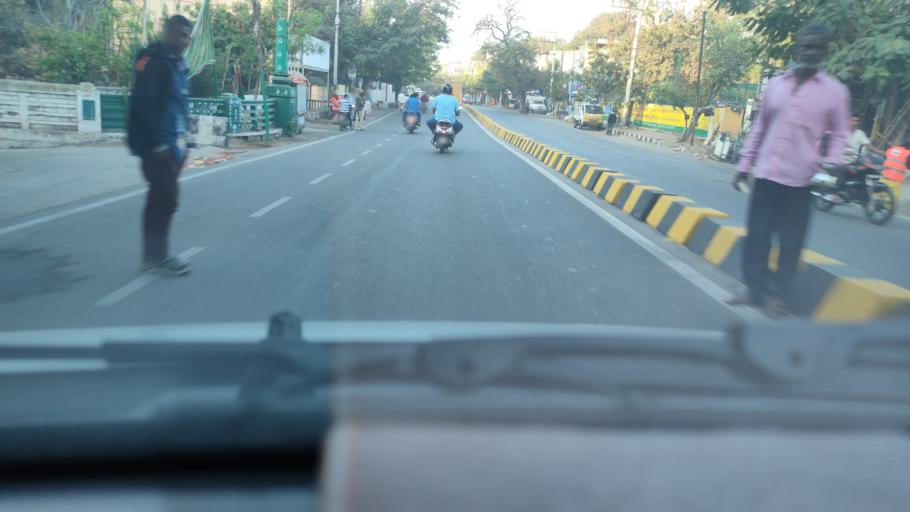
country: IN
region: Telangana
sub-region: Rangareddi
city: Gaddi Annaram
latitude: 17.4051
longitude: 78.5128
